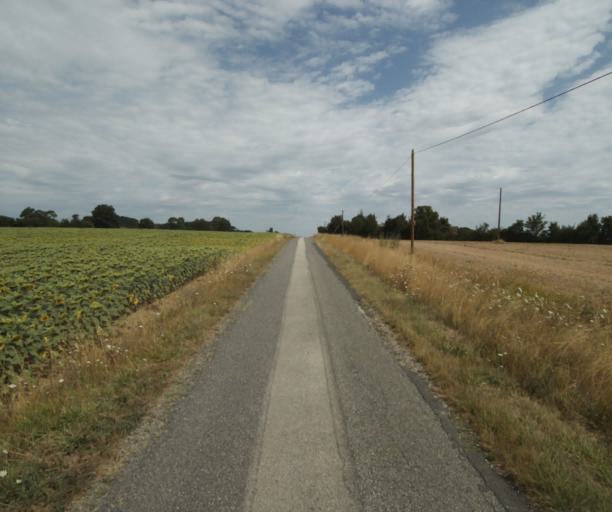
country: FR
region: Midi-Pyrenees
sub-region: Departement de la Haute-Garonne
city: Saint-Felix-Lauragais
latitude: 43.4377
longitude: 1.9051
